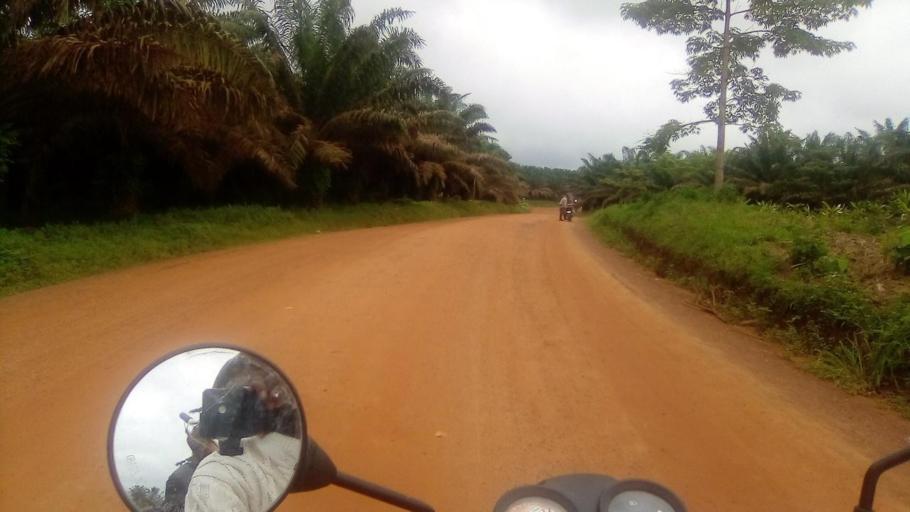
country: SL
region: Southern Province
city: Tongole
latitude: 7.4326
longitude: -11.8469
